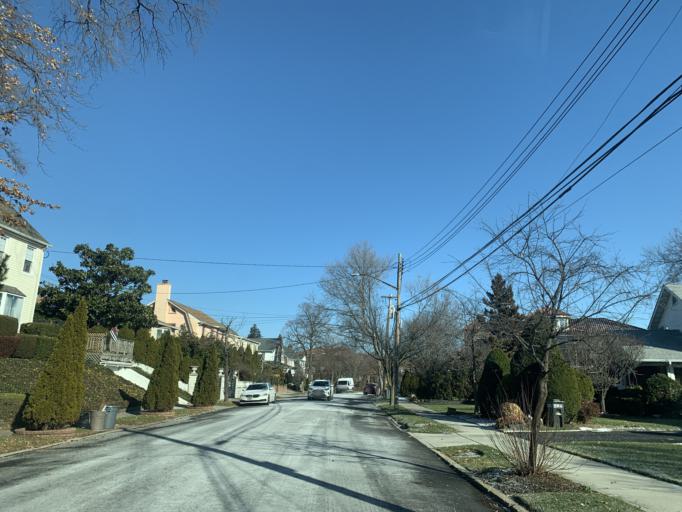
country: US
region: New York
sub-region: Bronx
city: The Bronx
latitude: 40.7899
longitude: -73.8286
